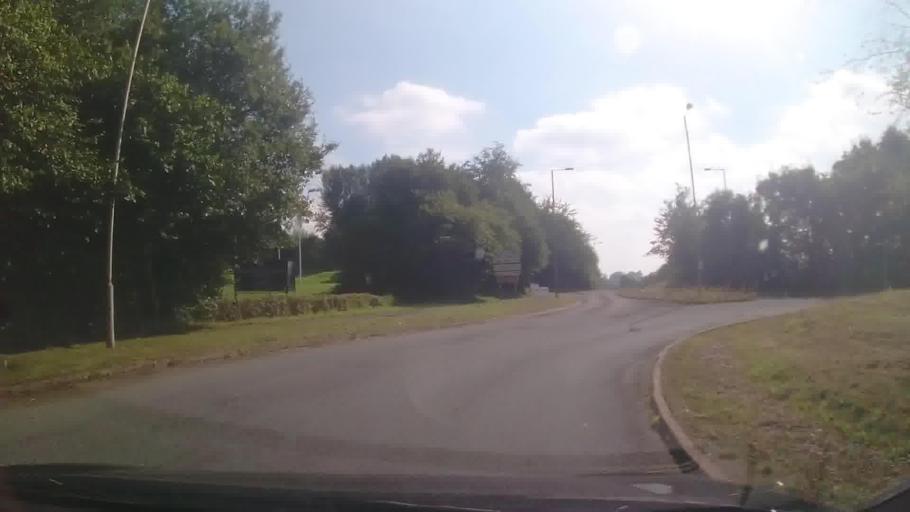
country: GB
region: England
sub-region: Shropshire
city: Whitchurch
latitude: 52.9831
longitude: -2.6905
